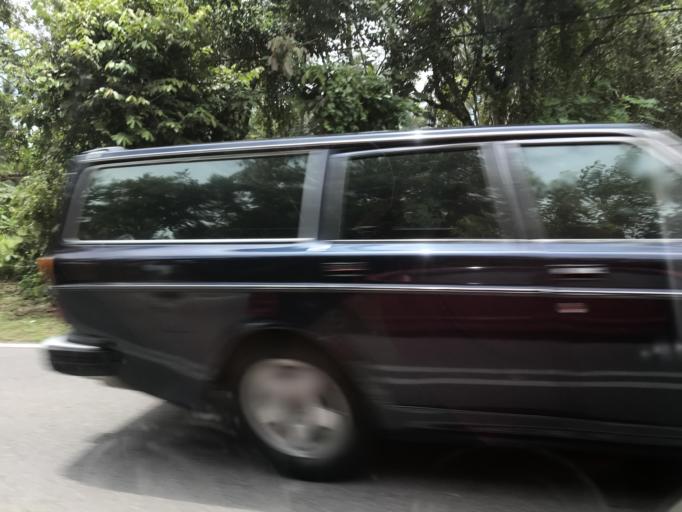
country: MY
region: Kelantan
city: Tumpat
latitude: 6.1737
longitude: 102.2019
